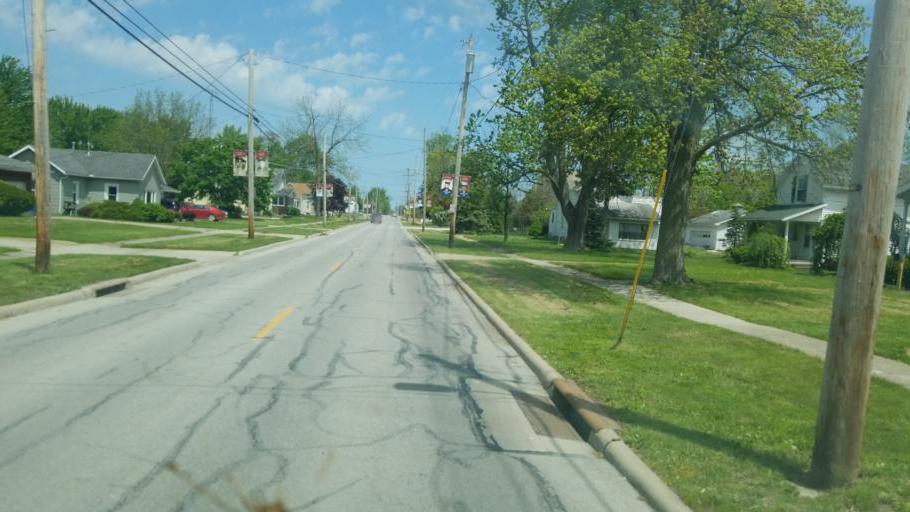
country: US
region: Ohio
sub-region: Ottawa County
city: Oak Harbor
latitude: 41.5178
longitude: -83.1450
